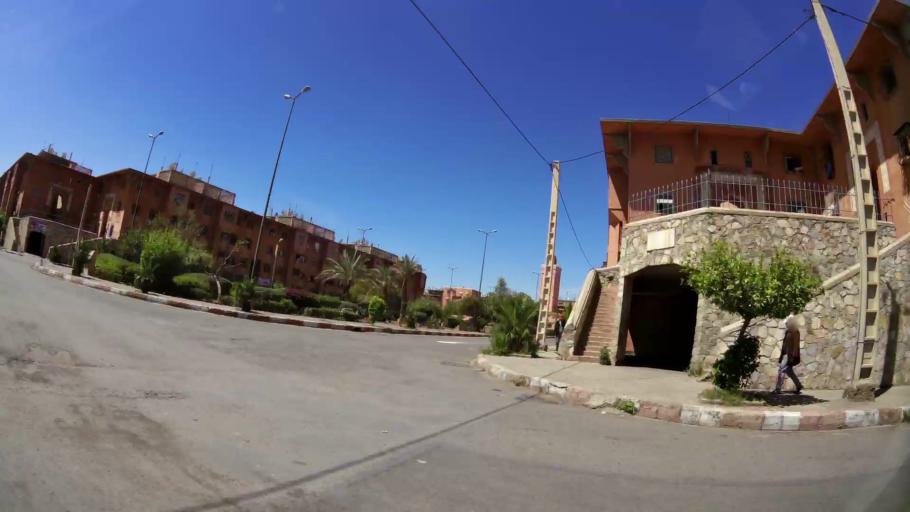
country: MA
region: Marrakech-Tensift-Al Haouz
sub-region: Marrakech
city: Marrakesh
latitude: 31.6345
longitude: -8.0638
